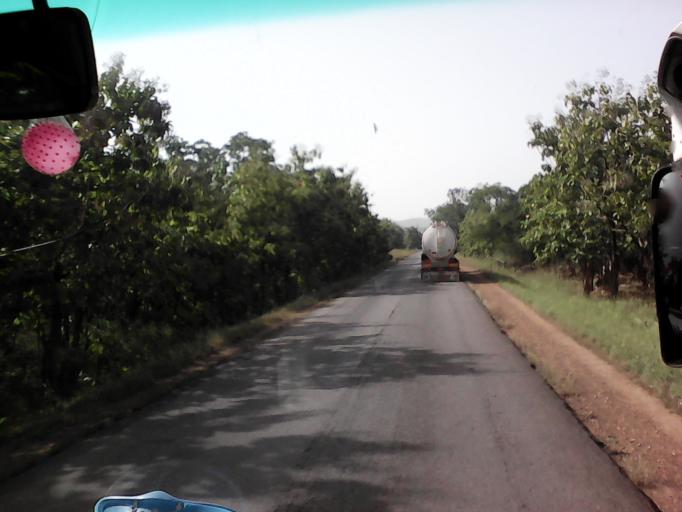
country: TG
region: Centrale
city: Sokode
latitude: 9.0850
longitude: 1.1358
